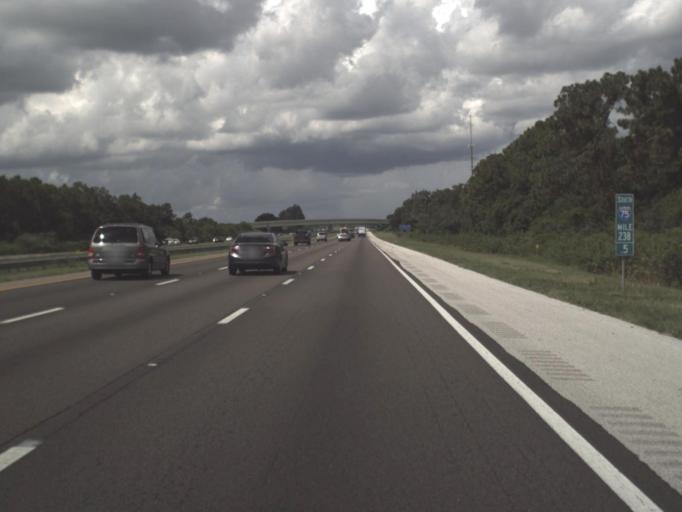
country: US
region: Florida
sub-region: Hillsborough County
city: Ruskin
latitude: 27.6979
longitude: -82.4038
